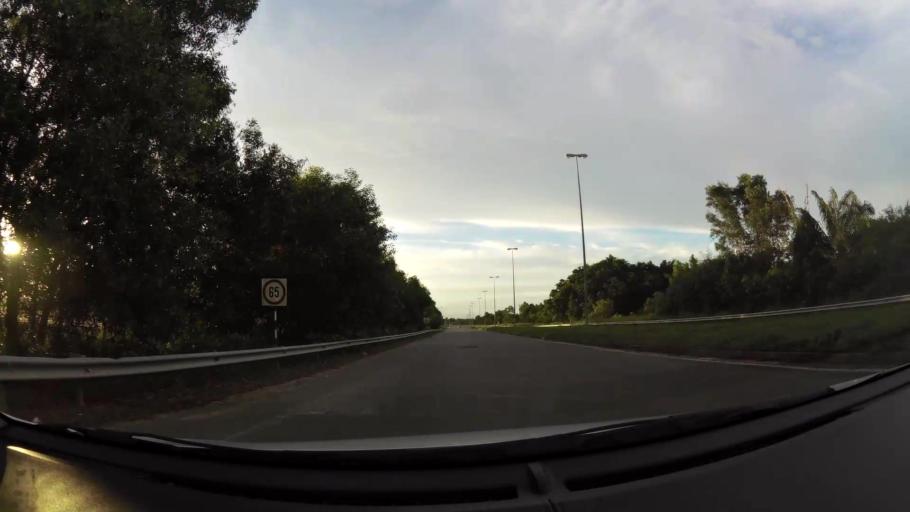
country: BN
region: Brunei and Muara
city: Bandar Seri Begawan
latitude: 4.9858
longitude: 114.9909
